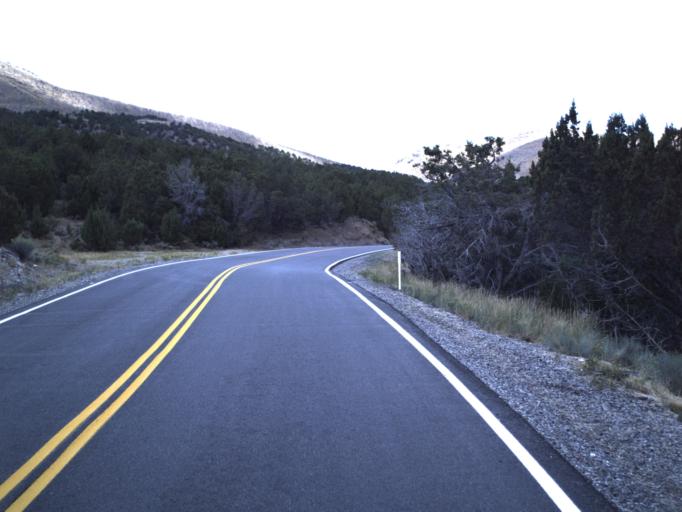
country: US
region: Utah
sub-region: Tooele County
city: Grantsville
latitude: 40.3397
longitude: -112.5761
